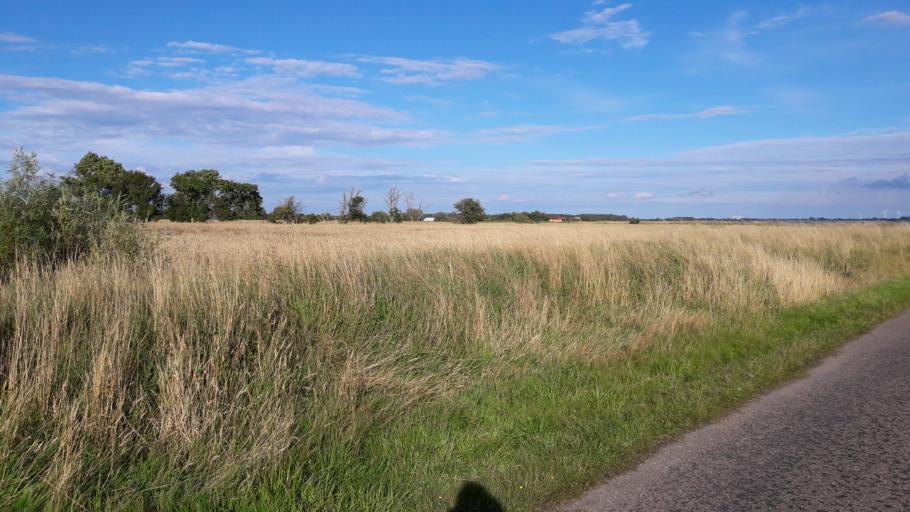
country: DK
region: South Denmark
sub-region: AEro Kommune
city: AEroskobing
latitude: 55.0047
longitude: 10.4732
